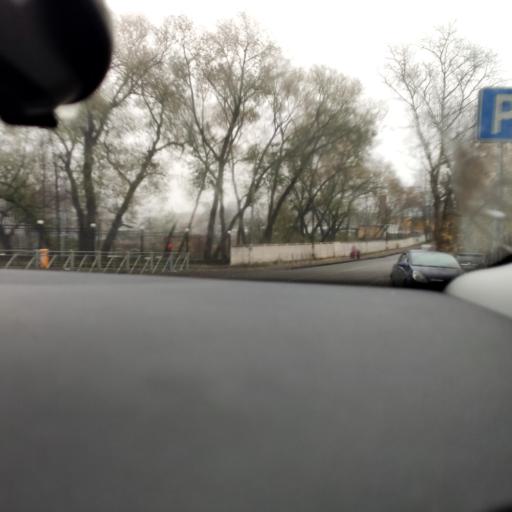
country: RU
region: Moskovskaya
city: Nakhabino
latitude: 55.8412
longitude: 37.1625
